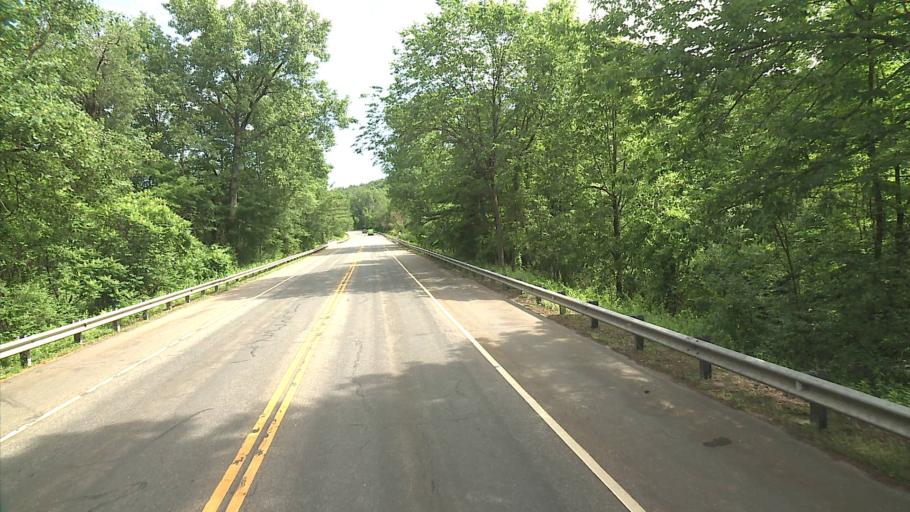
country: US
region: Connecticut
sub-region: Litchfield County
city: Canaan
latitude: 41.9166
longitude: -73.2735
